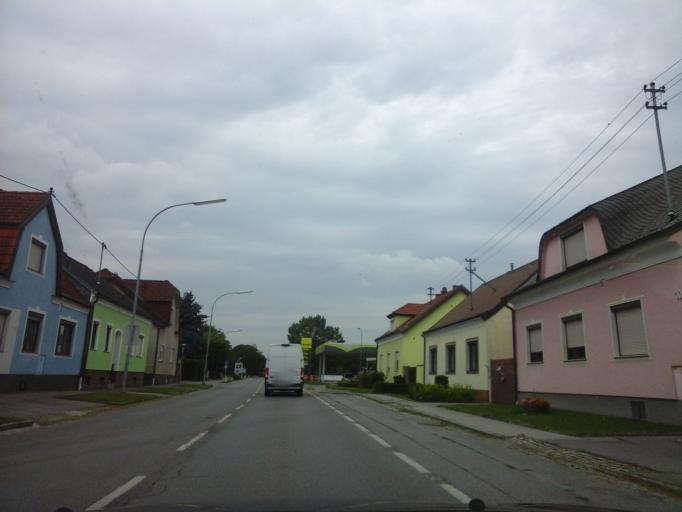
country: AT
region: Lower Austria
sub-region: Politischer Bezirk Ganserndorf
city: Orth an der Donau
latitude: 48.1499
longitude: 16.6888
